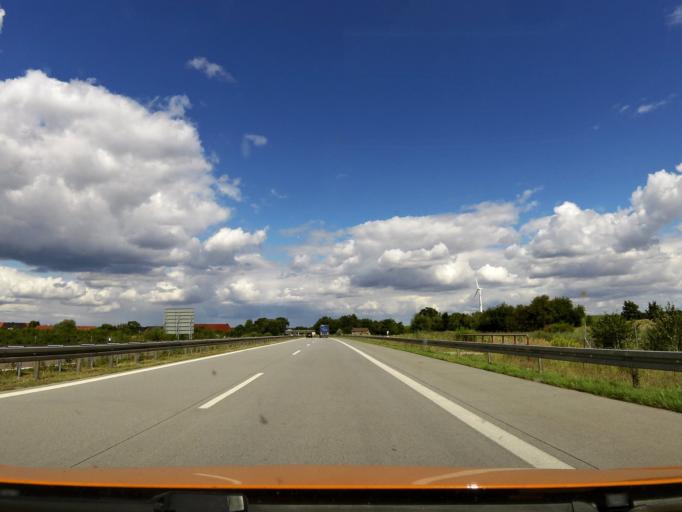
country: DE
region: Brandenburg
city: Althuttendorf
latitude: 52.9589
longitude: 13.8110
